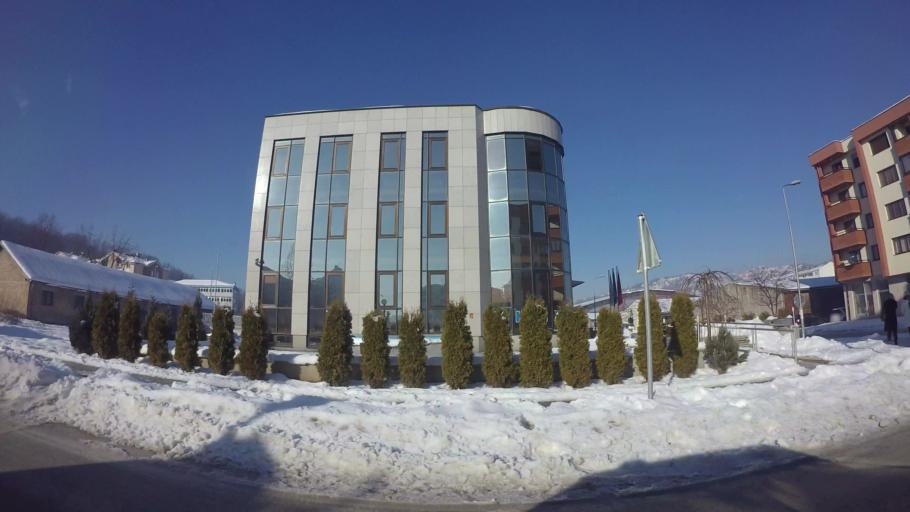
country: BA
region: Federation of Bosnia and Herzegovina
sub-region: Kanton Sarajevo
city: Sarajevo
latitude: 43.8252
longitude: 18.3691
